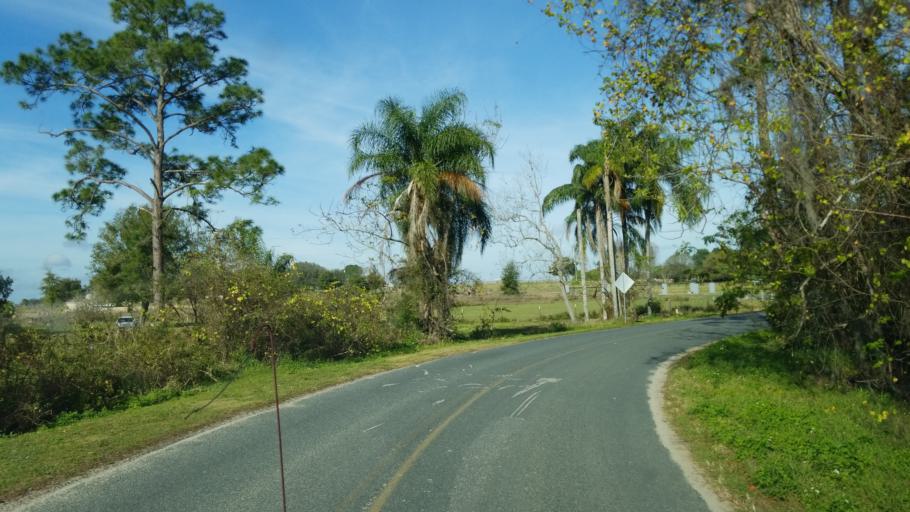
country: US
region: Florida
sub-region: Lake County
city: Clermont
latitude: 28.4445
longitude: -81.7922
